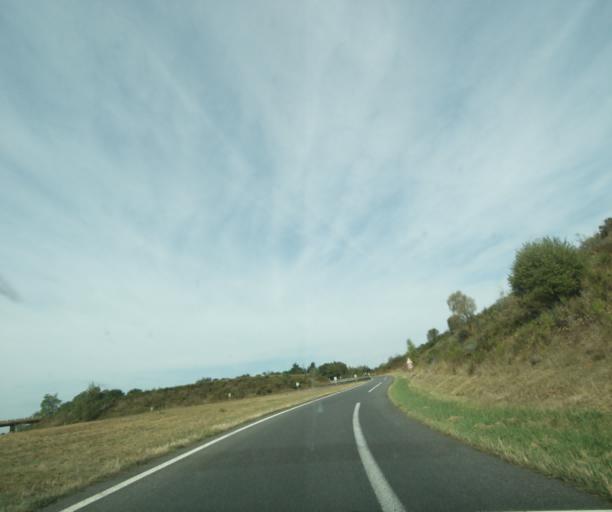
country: FR
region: Auvergne
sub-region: Departement de l'Allier
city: Molinet
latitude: 46.4562
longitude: 3.9179
